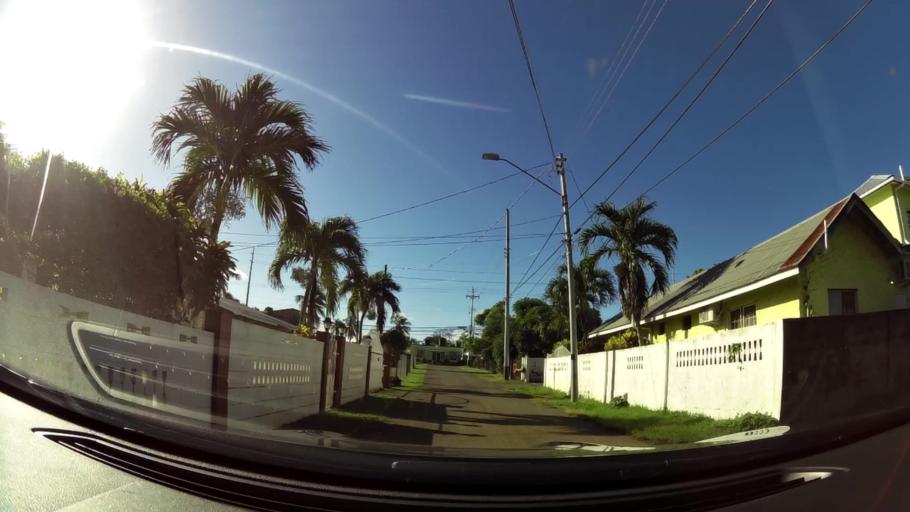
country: TT
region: Tobago
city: Scarborough
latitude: 11.1544
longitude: -60.8354
